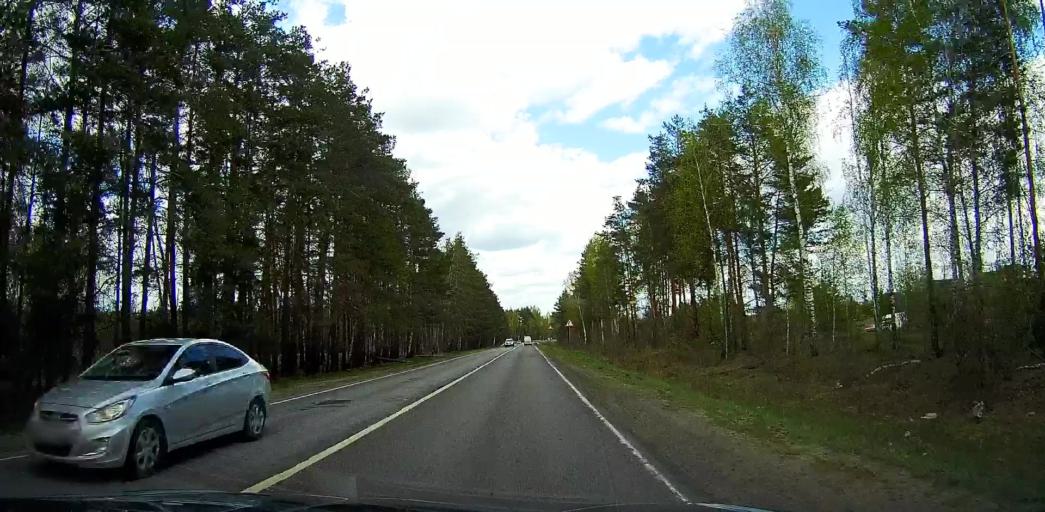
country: RU
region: Moskovskaya
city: Davydovo
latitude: 55.6271
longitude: 38.8614
